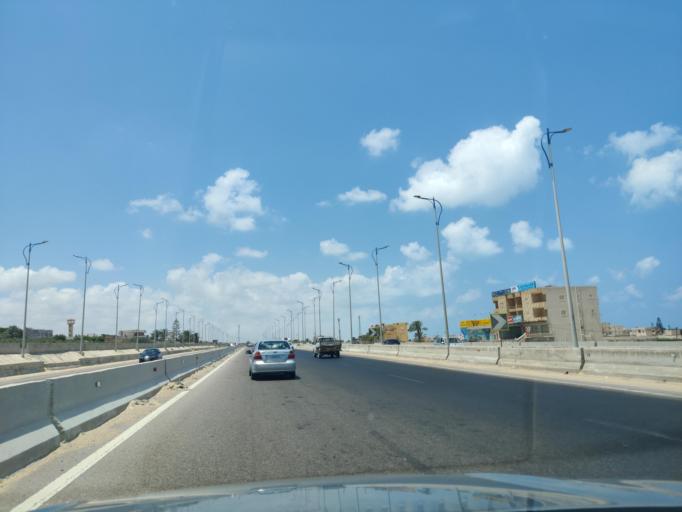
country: EG
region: Alexandria
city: Alexandria
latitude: 30.9722
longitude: 29.5654
